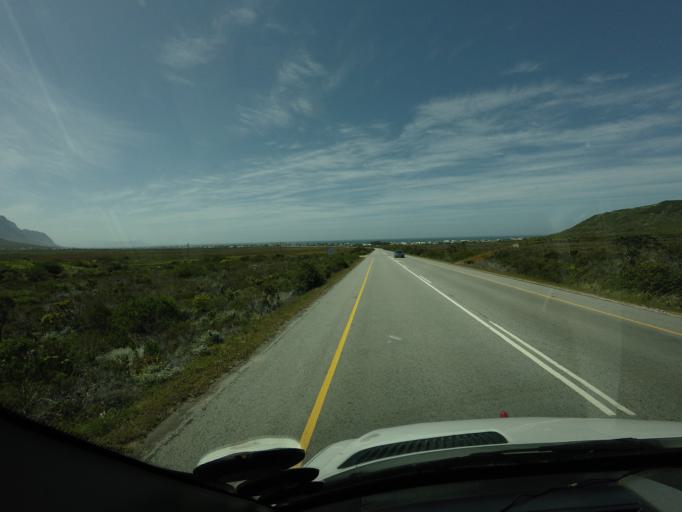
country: ZA
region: Western Cape
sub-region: Overberg District Municipality
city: Grabouw
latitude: -34.3556
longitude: 18.8604
